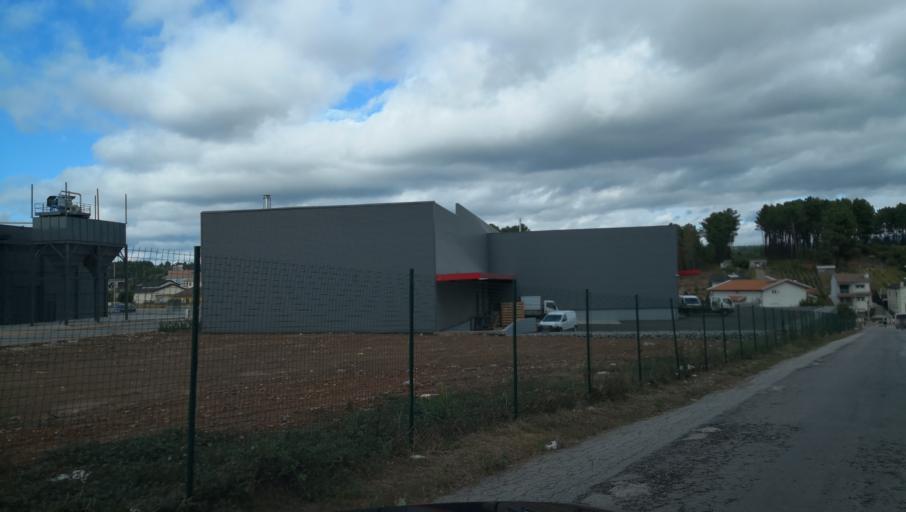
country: PT
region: Vila Real
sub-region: Vila Real
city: Vila Real
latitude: 41.2680
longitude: -7.6945
